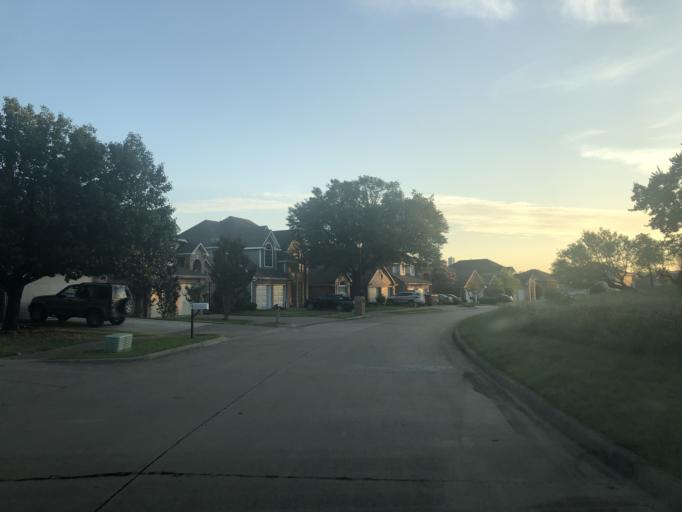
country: US
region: Texas
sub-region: Dallas County
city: Cedar Hill
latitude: 32.6489
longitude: -96.9720
